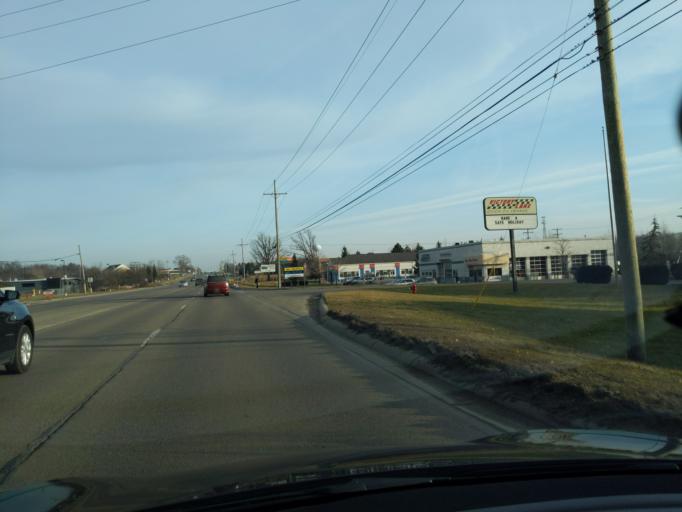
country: US
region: Michigan
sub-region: Livingston County
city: Howell
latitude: 42.5935
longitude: -83.8926
